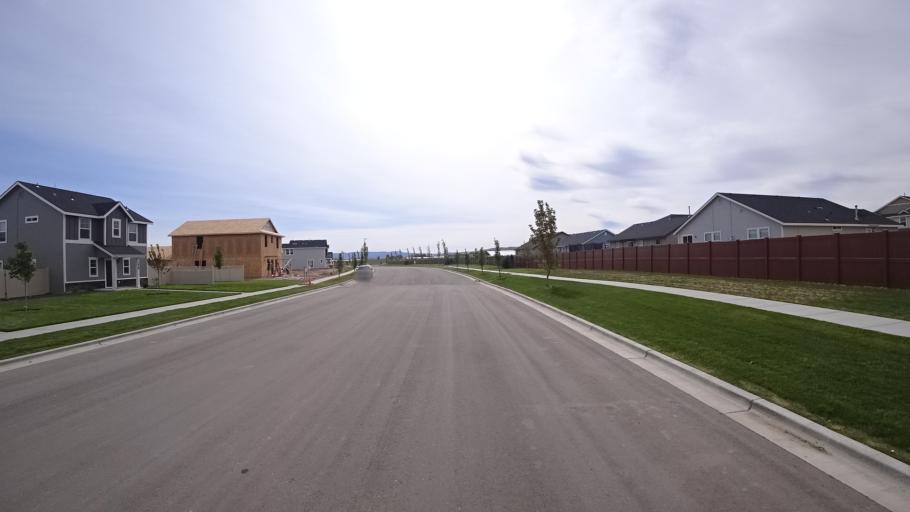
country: US
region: Idaho
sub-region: Ada County
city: Garden City
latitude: 43.5330
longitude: -116.2977
